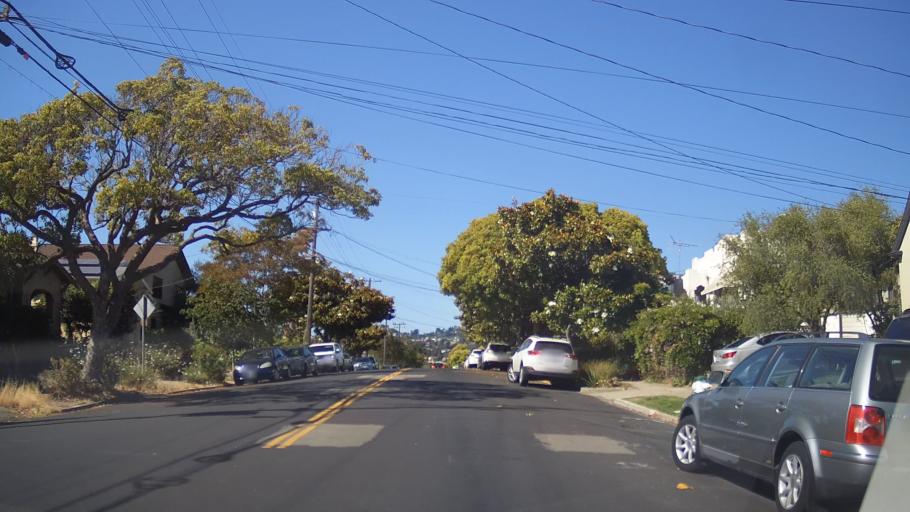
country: US
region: California
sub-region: Alameda County
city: Albany
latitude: 37.8839
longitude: -122.2866
